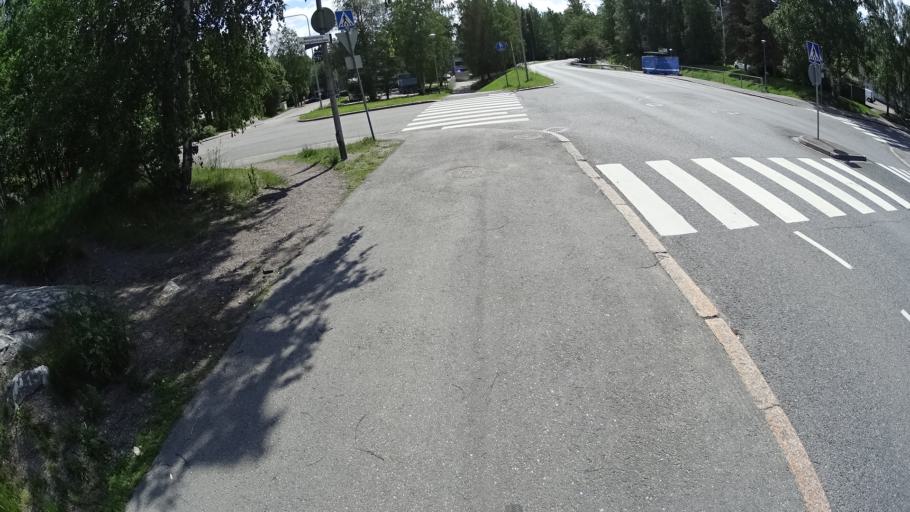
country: FI
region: Uusimaa
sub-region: Helsinki
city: Vantaa
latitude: 60.2359
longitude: 25.1268
